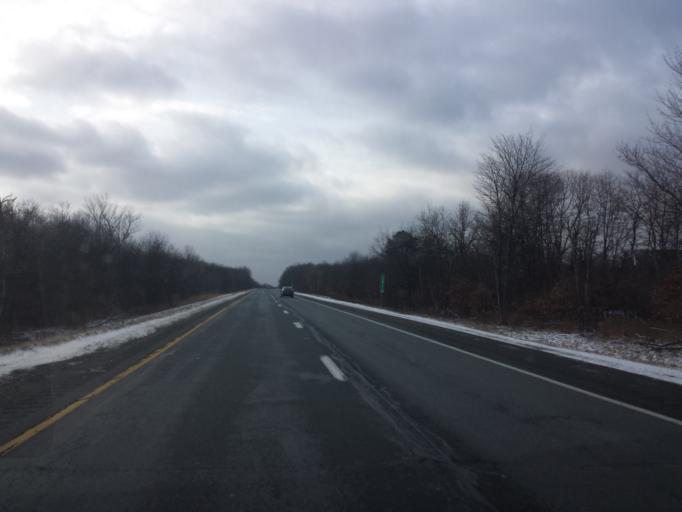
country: US
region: Pennsylvania
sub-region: Monroe County
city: Emerald Lakes
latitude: 41.0723
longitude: -75.4232
